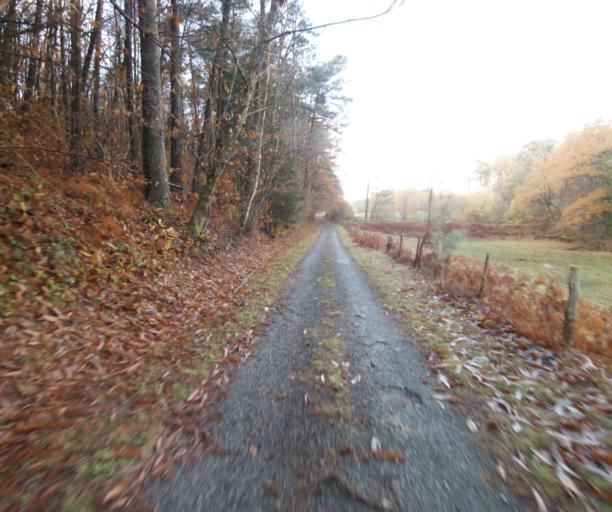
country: FR
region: Limousin
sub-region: Departement de la Correze
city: Cornil
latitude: 45.2159
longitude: 1.6787
